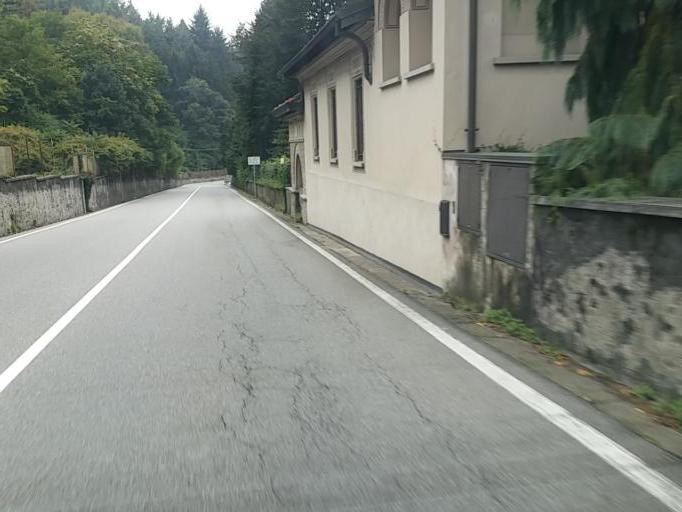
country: IT
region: Piedmont
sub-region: Provincia di Novara
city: Orta San Giulio
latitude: 45.7950
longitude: 8.4166
